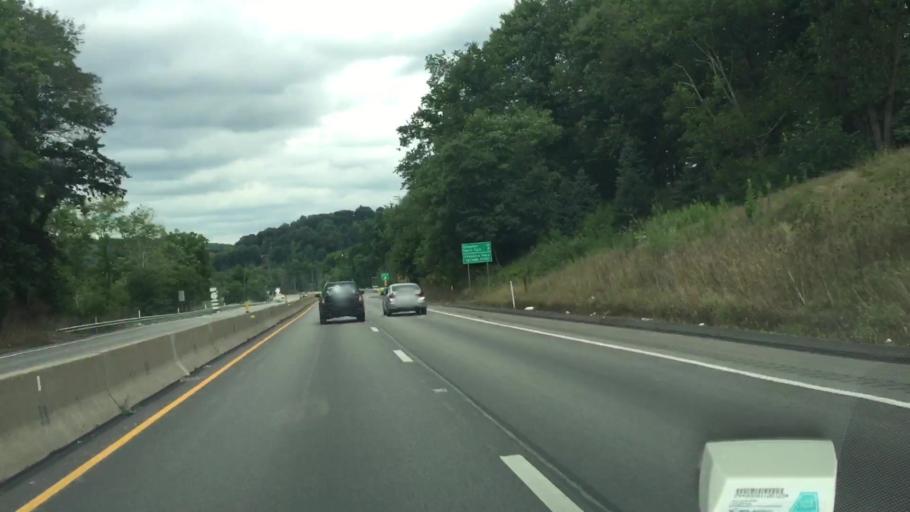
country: US
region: Pennsylvania
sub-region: Allegheny County
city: West View
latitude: 40.5767
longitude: -80.0338
